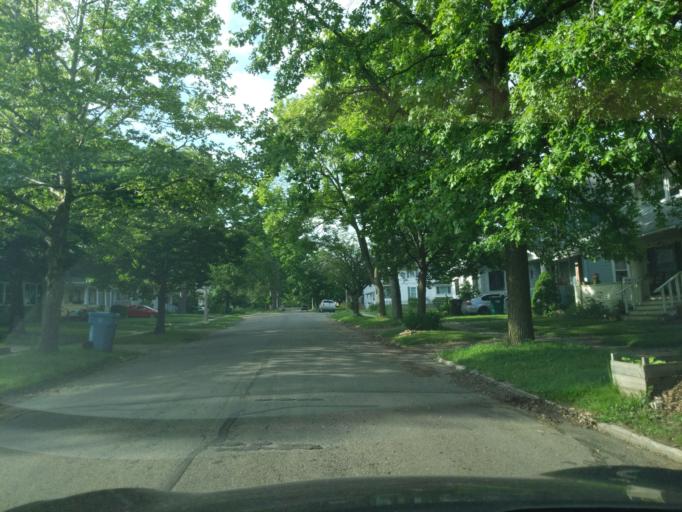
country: US
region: Michigan
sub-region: Ingham County
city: Lansing
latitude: 42.7233
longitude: -84.5356
